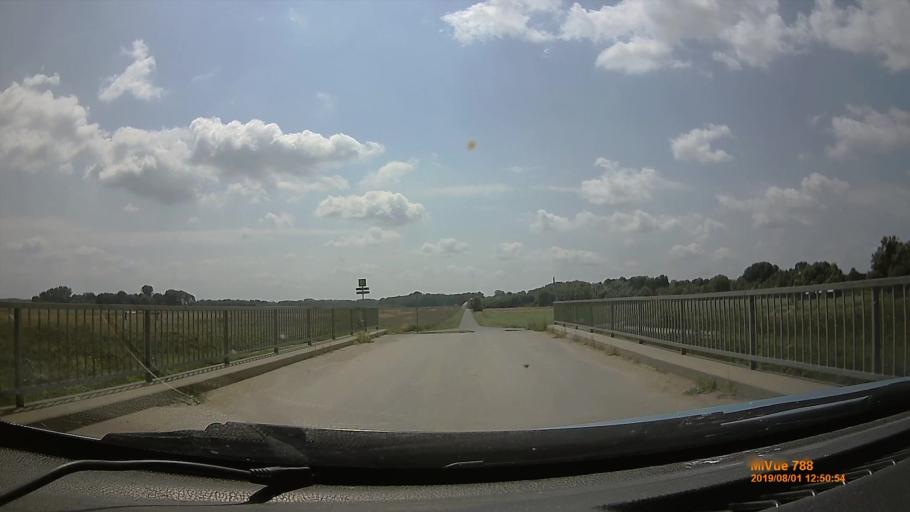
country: HR
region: Osjecko-Baranjska
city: Viljevo
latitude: 45.8070
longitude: 18.1025
